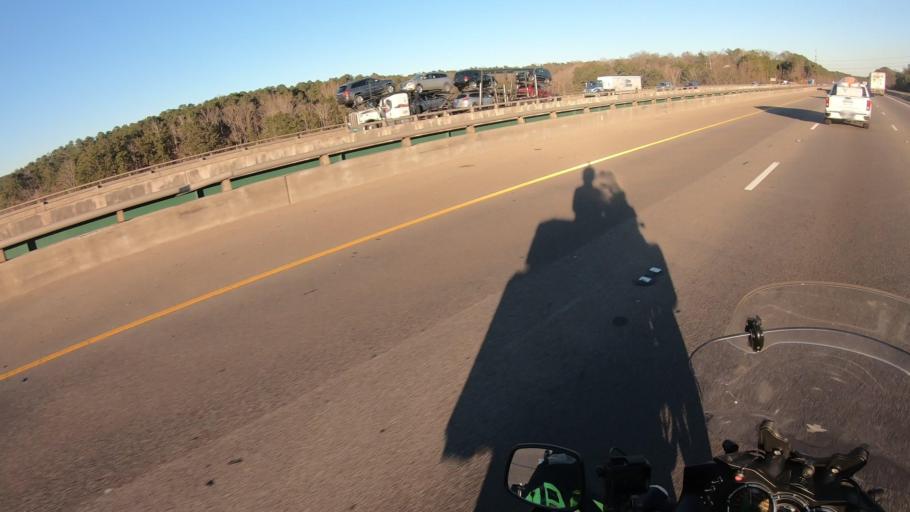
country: US
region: Georgia
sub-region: Cobb County
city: Acworth
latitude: 34.0893
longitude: -84.7135
